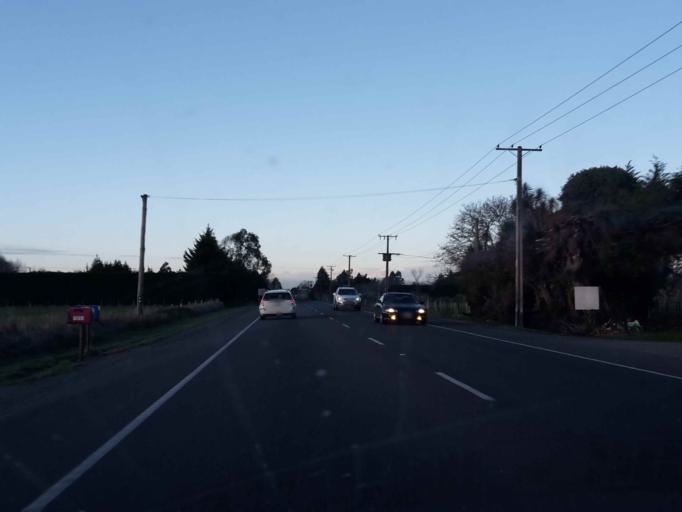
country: NZ
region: Canterbury
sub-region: Selwyn District
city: Rolleston
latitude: -43.5708
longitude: 172.4361
